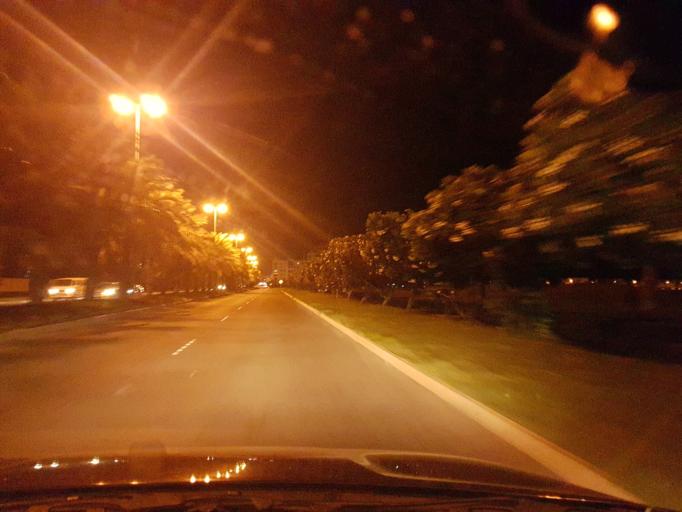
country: BH
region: Muharraq
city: Al Hadd
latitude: 26.2800
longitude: 50.6639
